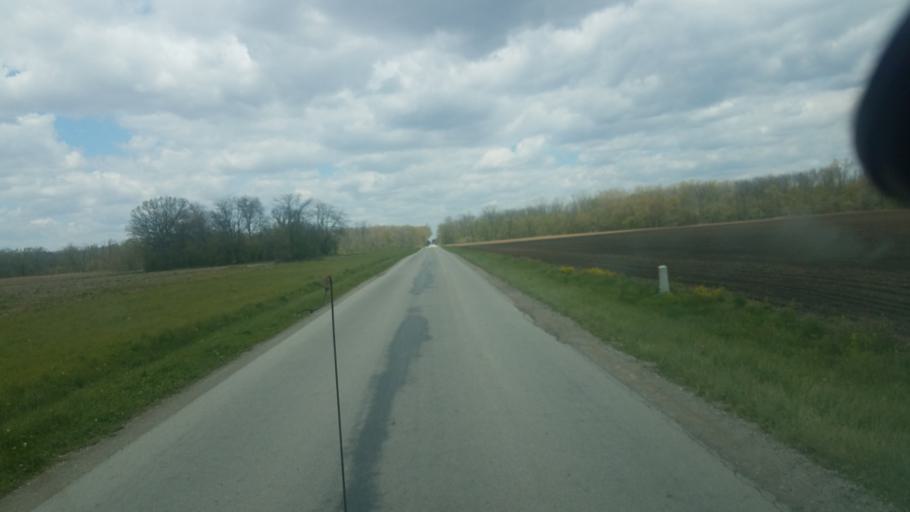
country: US
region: Ohio
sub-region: Marion County
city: Marion
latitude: 40.6971
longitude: -83.0923
